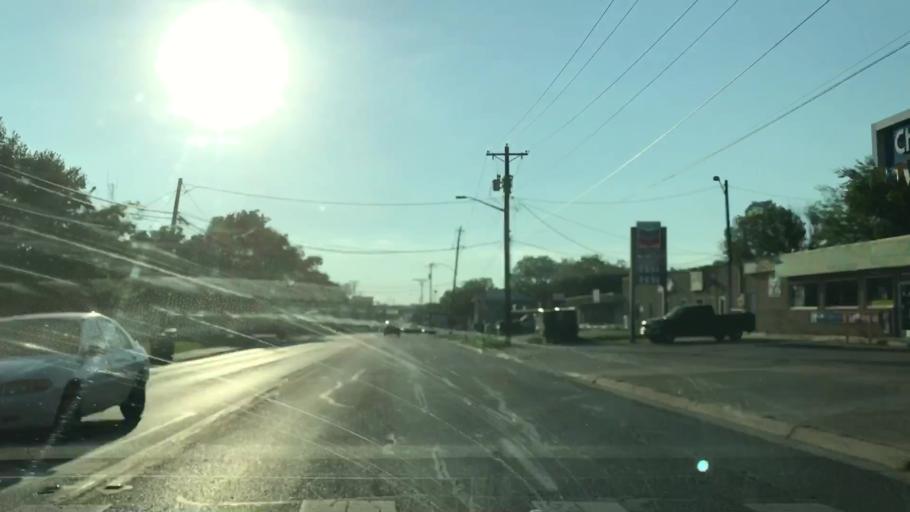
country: US
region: Texas
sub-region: Denton County
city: Denton
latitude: 33.2161
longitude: -97.1190
